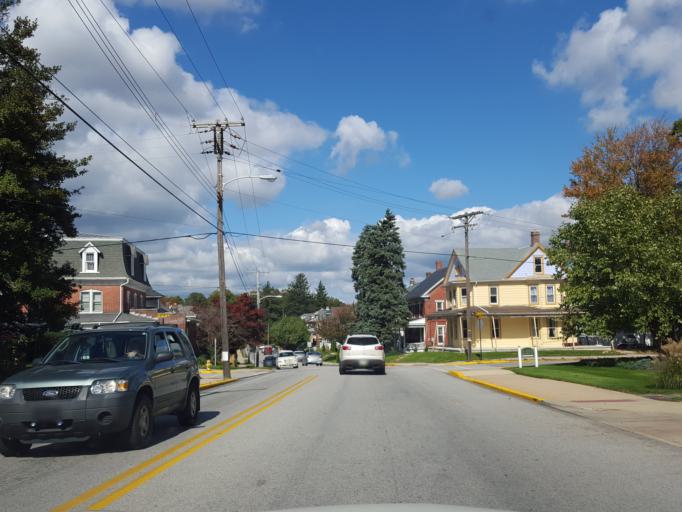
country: US
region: Pennsylvania
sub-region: York County
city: Red Lion
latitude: 39.9039
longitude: -76.6095
